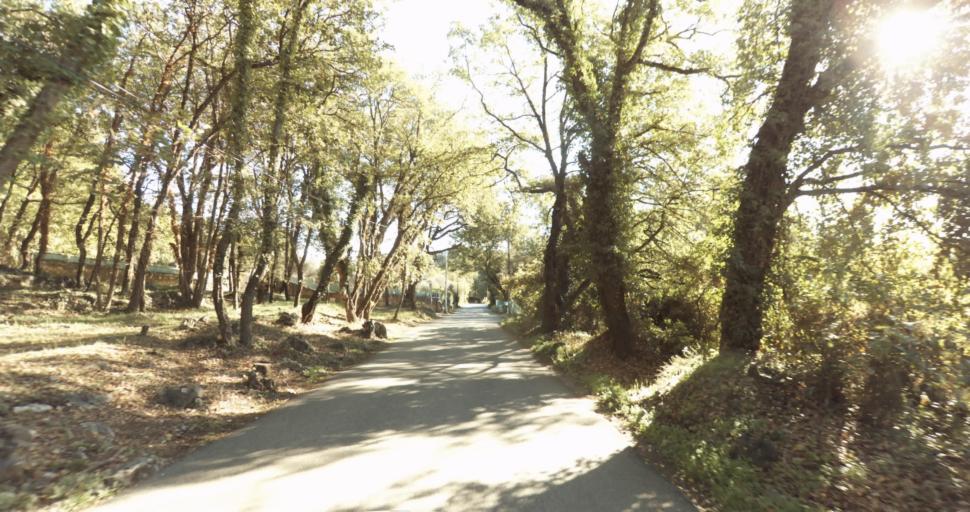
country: FR
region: Provence-Alpes-Cote d'Azur
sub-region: Departement des Alpes-Maritimes
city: Vence
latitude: 43.7119
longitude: 7.1017
